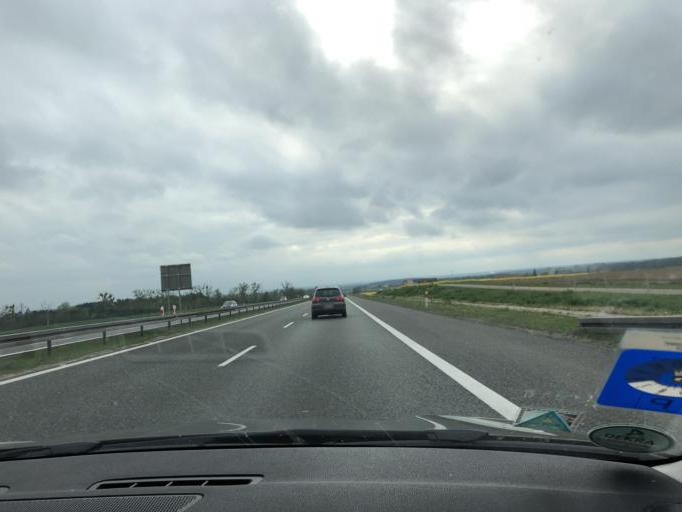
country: PL
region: Opole Voivodeship
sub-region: Powiat krapkowicki
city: Rozwadza
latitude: 50.4814
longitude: 18.1099
